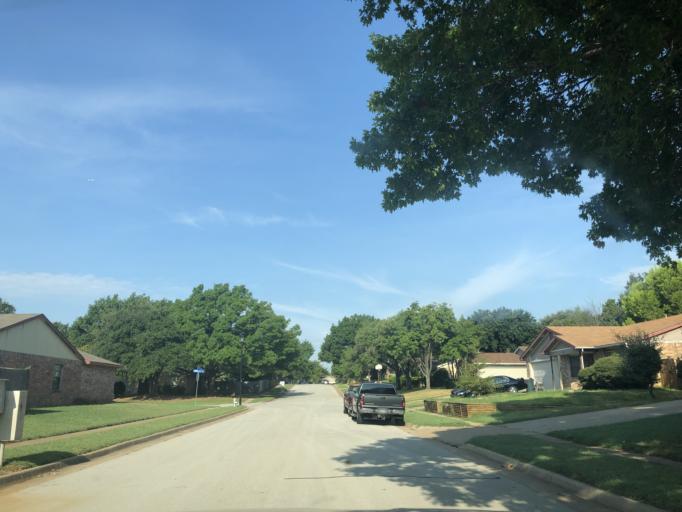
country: US
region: Texas
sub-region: Tarrant County
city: Euless
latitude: 32.8752
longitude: -97.0879
